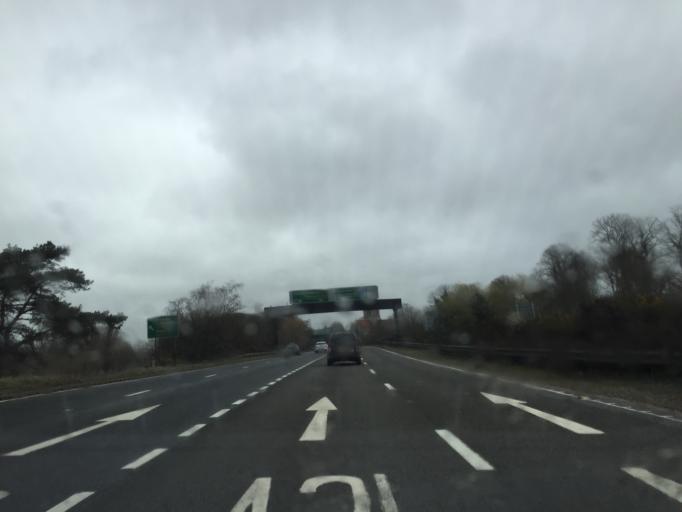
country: GB
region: England
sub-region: Hampshire
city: Ringwood
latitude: 50.8460
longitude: -1.8003
